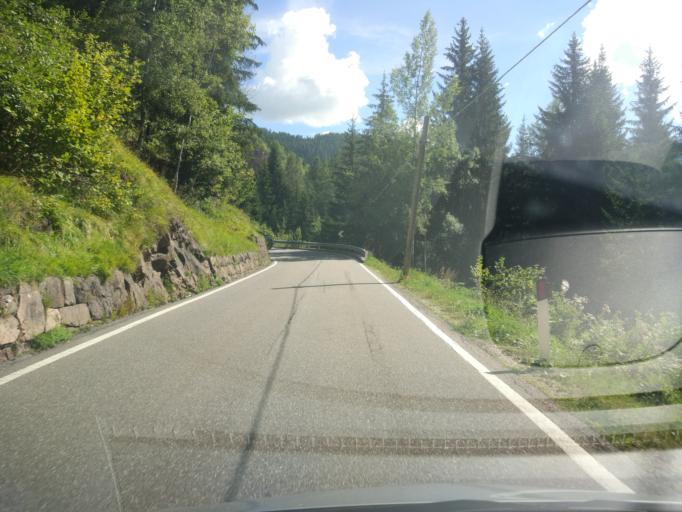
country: IT
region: Trentino-Alto Adige
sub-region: Provincia di Trento
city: Moena
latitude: 46.3071
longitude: 11.6973
